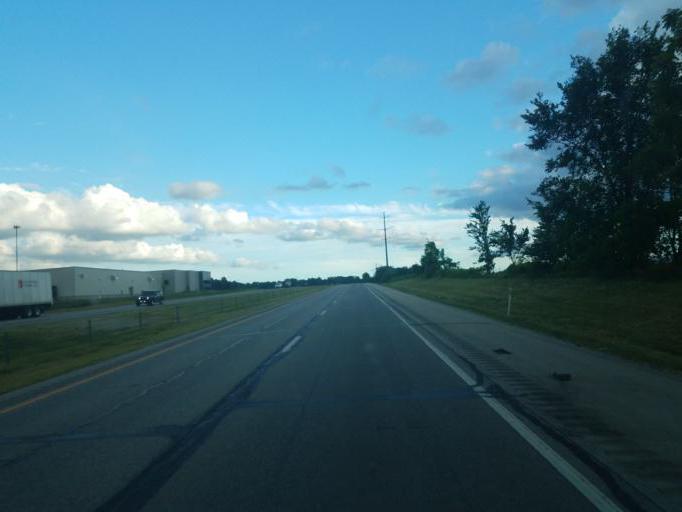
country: US
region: Indiana
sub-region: Allen County
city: Leo-Cedarville
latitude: 41.2693
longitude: -85.0871
